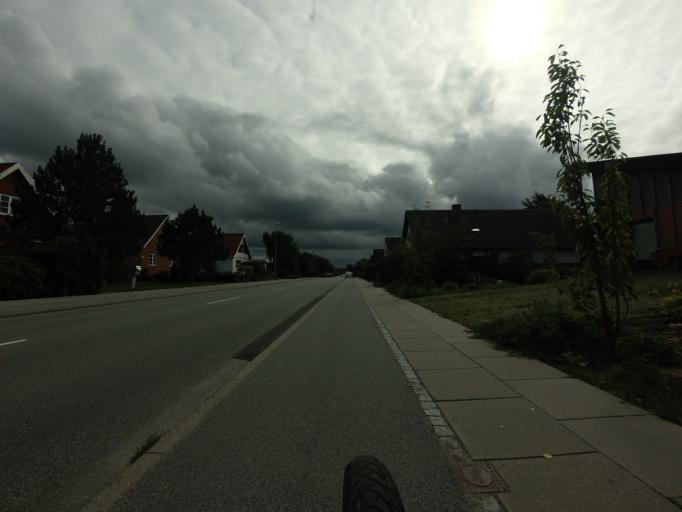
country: DK
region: North Denmark
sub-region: Hjorring Kommune
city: Hjorring
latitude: 57.4804
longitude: 9.9916
